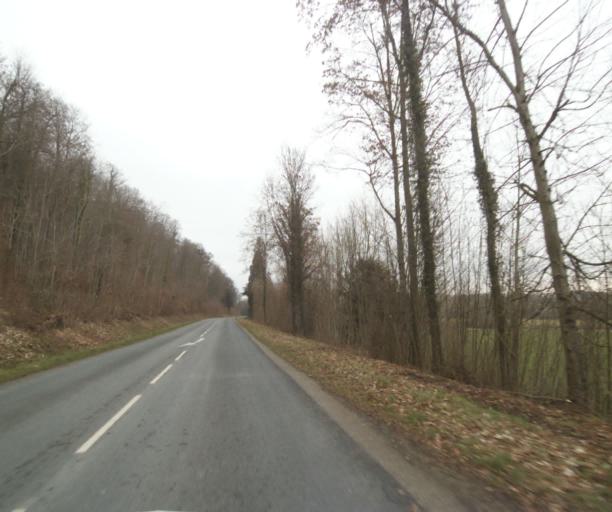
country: FR
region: Champagne-Ardenne
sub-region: Departement de la Haute-Marne
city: Bienville
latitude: 48.5739
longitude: 5.0379
